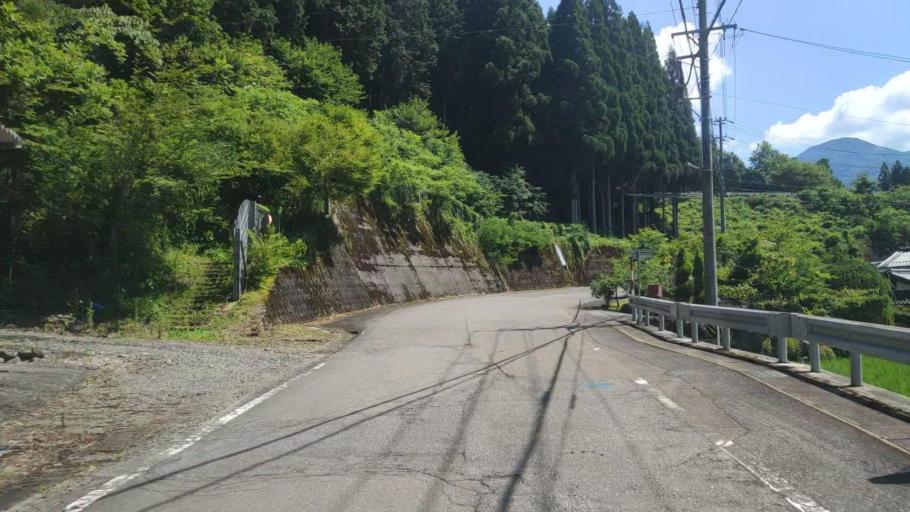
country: JP
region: Gifu
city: Godo
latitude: 35.6688
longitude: 136.5781
